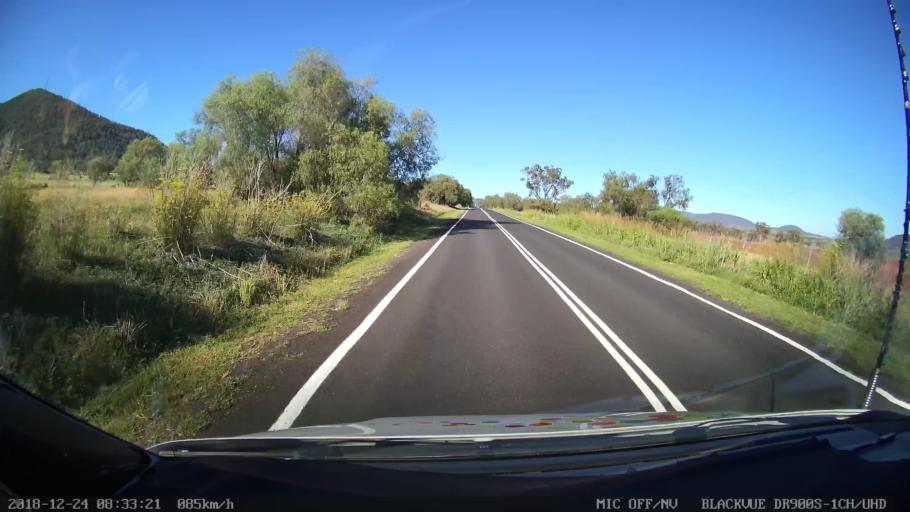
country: AU
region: New South Wales
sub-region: Liverpool Plains
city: Quirindi
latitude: -31.2858
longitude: 150.6856
